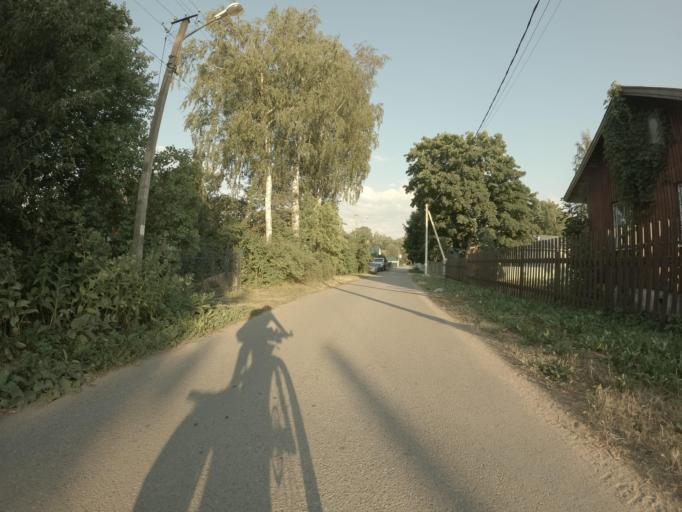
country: RU
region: Leningrad
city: Koltushi
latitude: 59.8890
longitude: 30.7096
